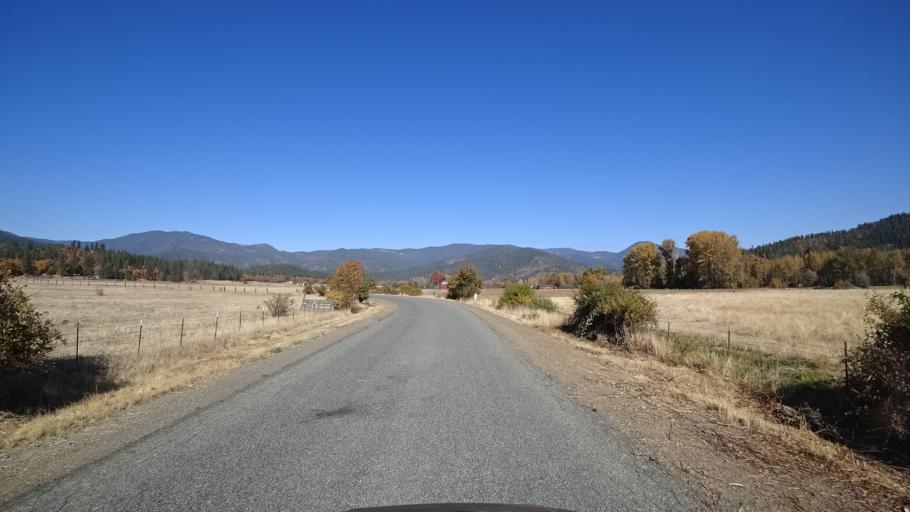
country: US
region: California
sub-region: Siskiyou County
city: Yreka
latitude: 41.6132
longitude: -122.9698
